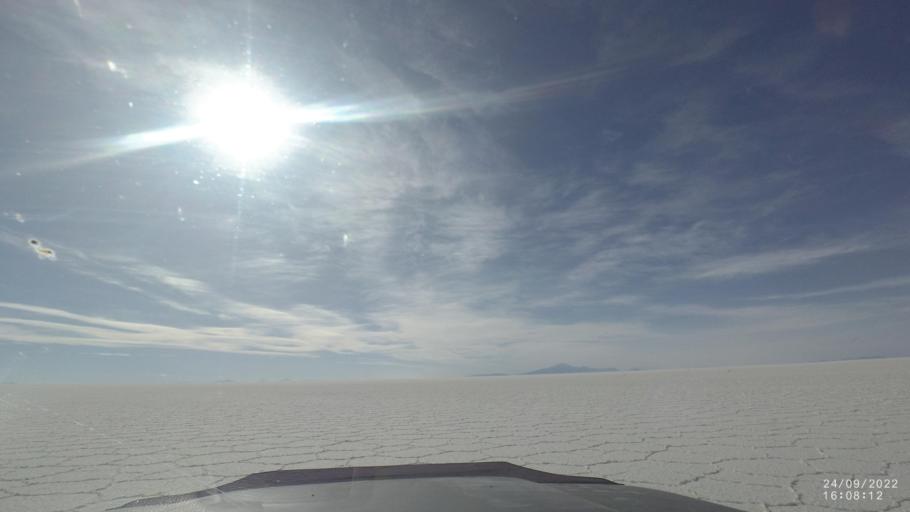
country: BO
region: Potosi
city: Colchani
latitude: -20.2946
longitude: -67.3095
